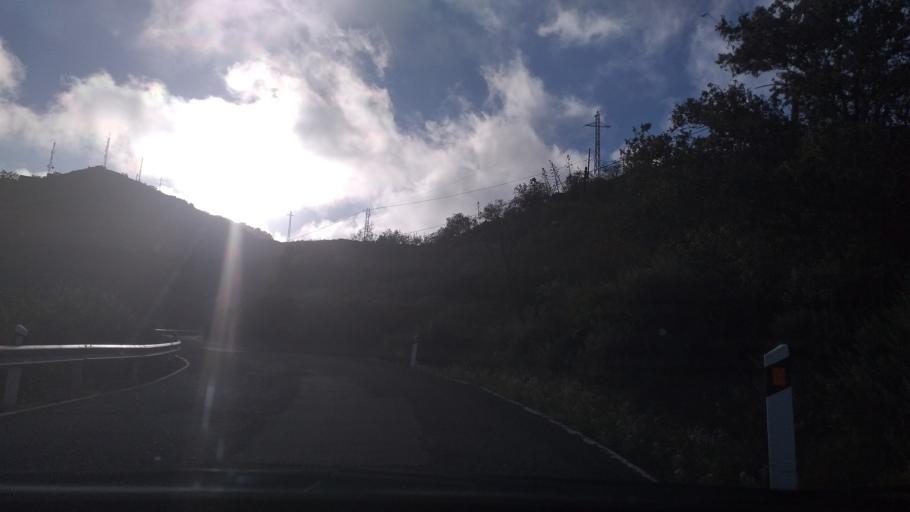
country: ES
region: Canary Islands
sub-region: Provincia de Las Palmas
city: Valsequillo de Gran Canaria
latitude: 27.9586
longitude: -15.5002
